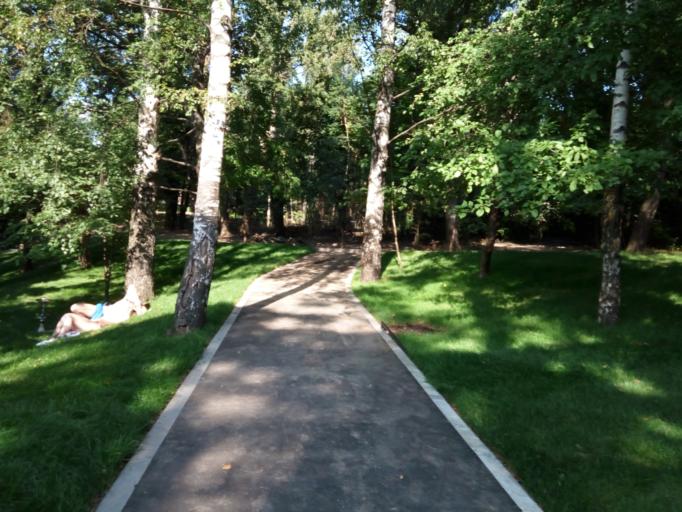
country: RU
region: Moskovskaya
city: Levoberezhnaya
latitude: 55.8783
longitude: 37.4604
